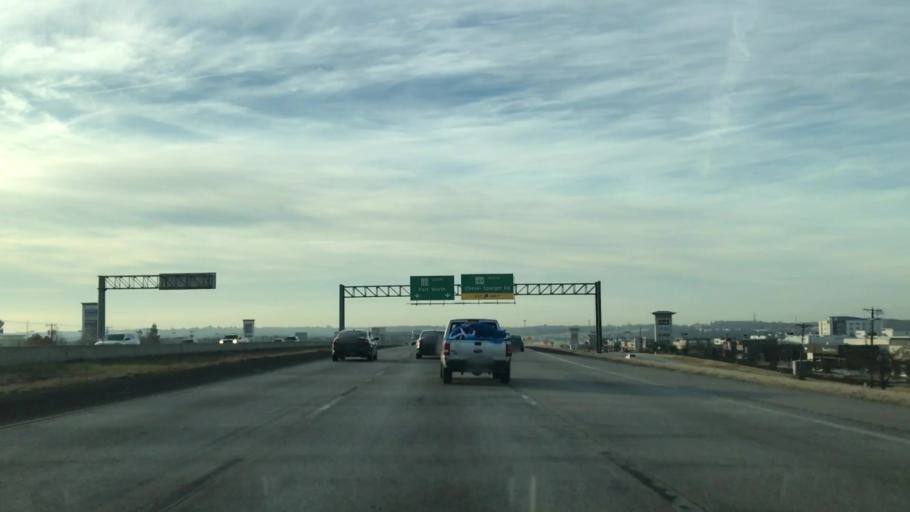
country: US
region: Texas
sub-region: Tarrant County
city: Euless
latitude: 32.8805
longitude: -97.0994
